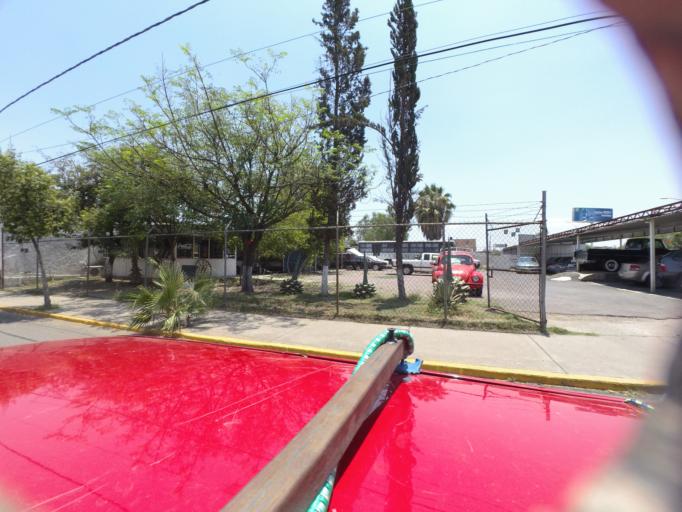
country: MX
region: Aguascalientes
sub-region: Aguascalientes
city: Aguascalientes
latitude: 21.8724
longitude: -102.2931
